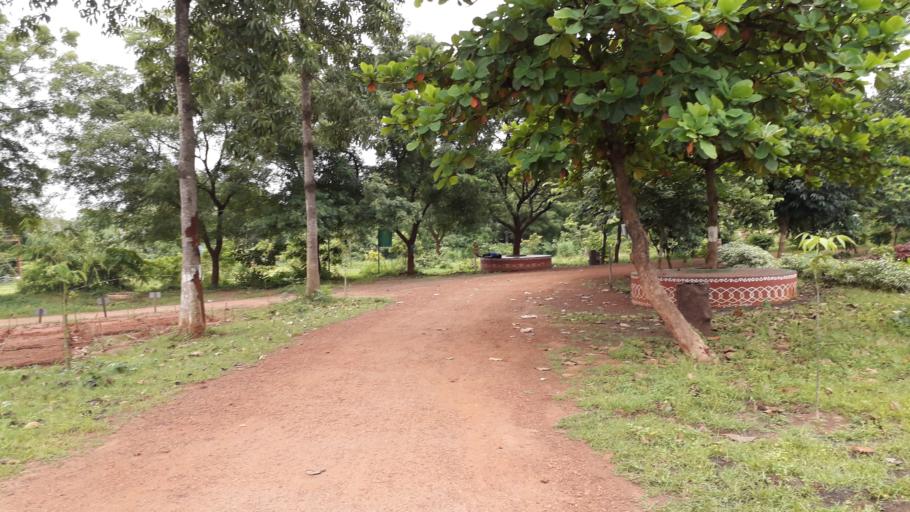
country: IN
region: Andhra Pradesh
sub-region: East Godavari
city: Rajahmundry
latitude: 17.0352
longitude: 81.8252
